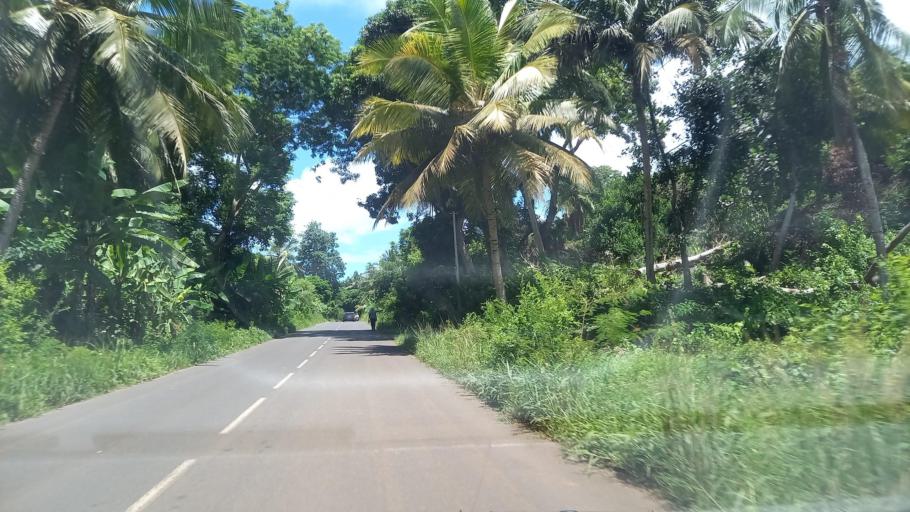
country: YT
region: Ouangani
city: Ouangani
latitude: -12.8771
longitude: 45.1230
